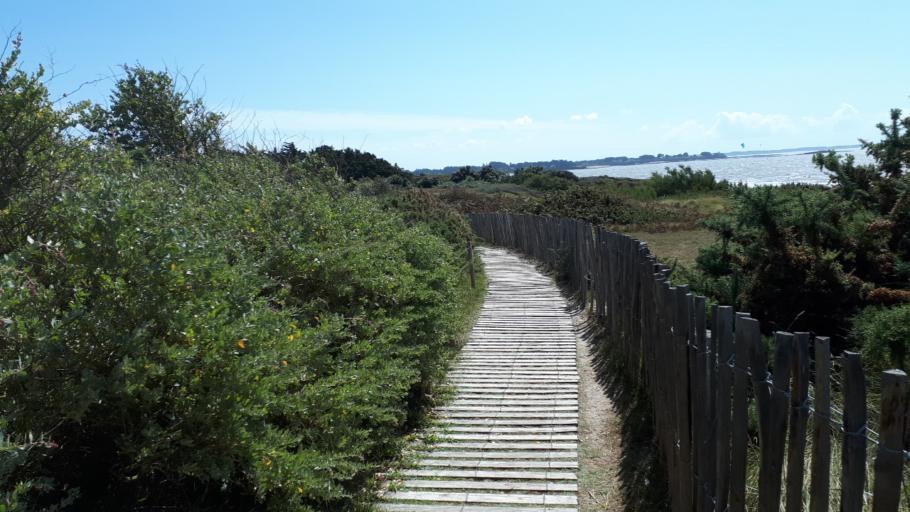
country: FR
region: Brittany
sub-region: Departement du Morbihan
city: Penestin
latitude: 47.4870
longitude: -2.4995
